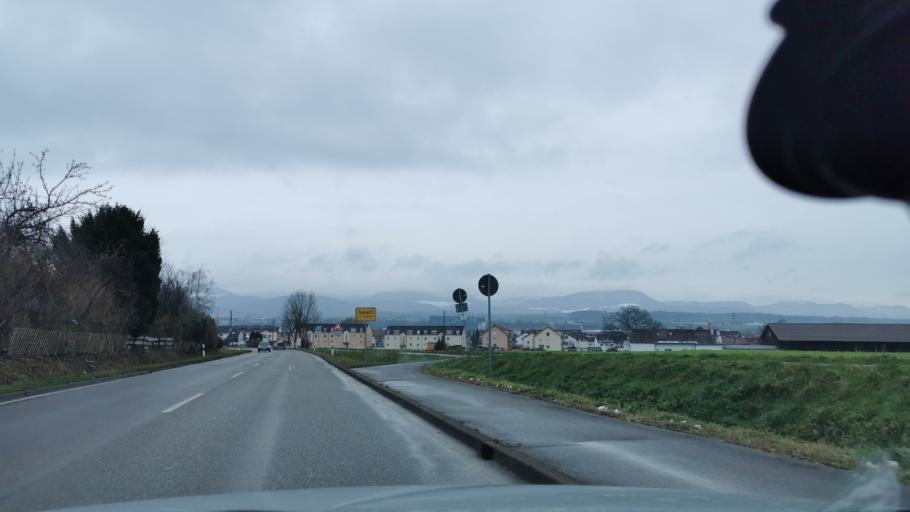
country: DE
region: Baden-Wuerttemberg
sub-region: Regierungsbezirk Stuttgart
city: Salach
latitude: 48.6978
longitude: 9.7357
